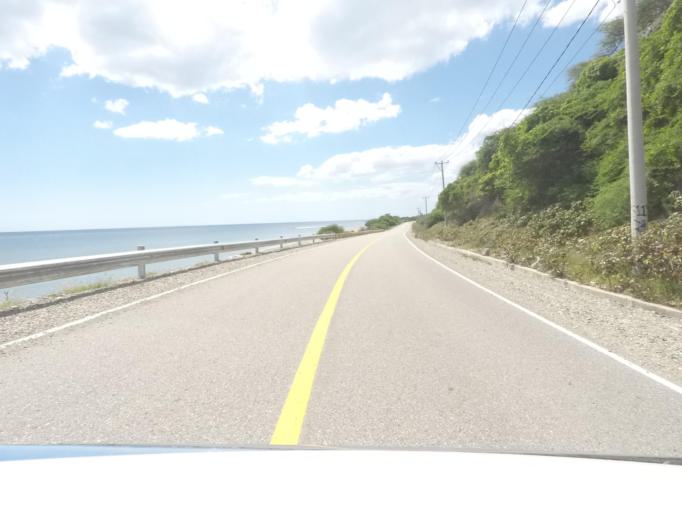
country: TL
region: Baucau
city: Baucau
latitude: -8.4099
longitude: 126.7207
